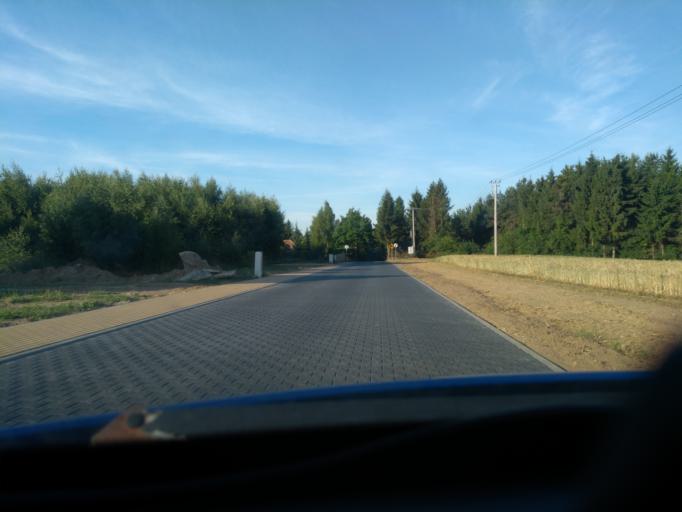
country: PL
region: Pomeranian Voivodeship
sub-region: Powiat kartuski
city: Przodkowo
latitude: 54.3856
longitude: 18.3186
